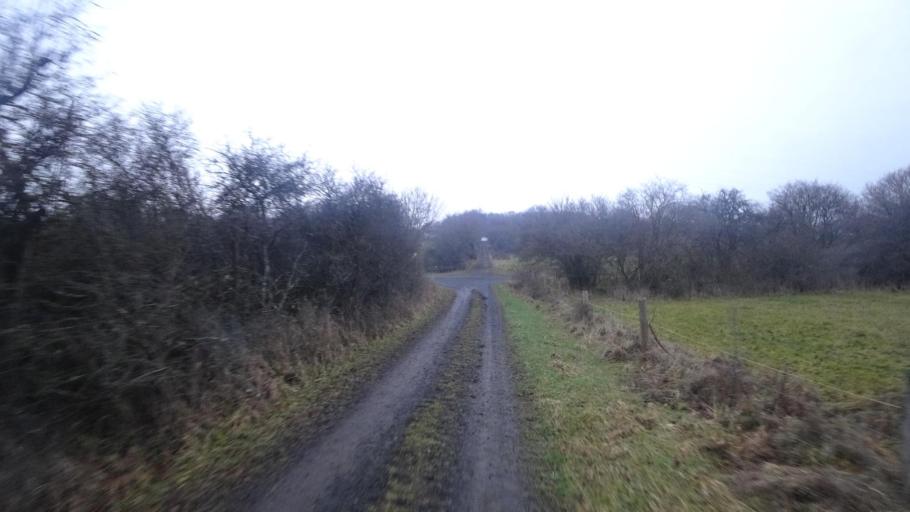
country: DE
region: Rheinland-Pfalz
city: Bellingen
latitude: 50.6006
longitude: 7.9101
